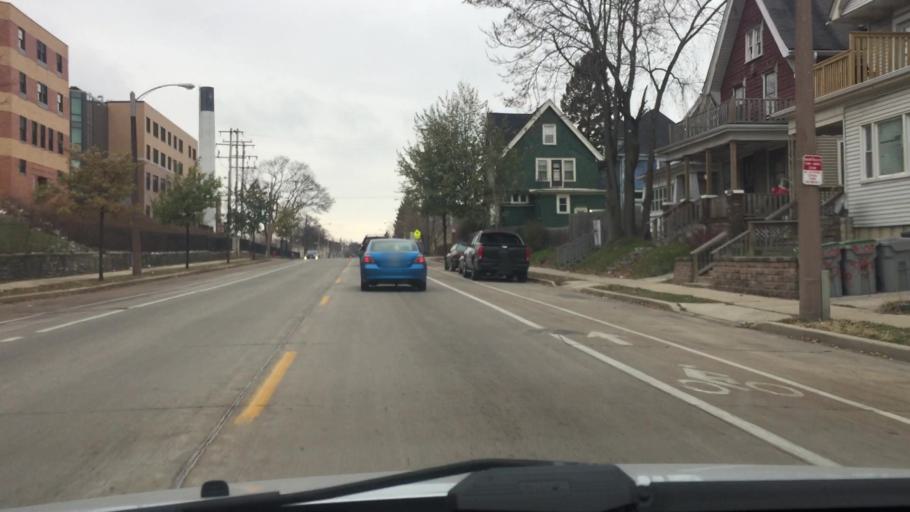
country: US
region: Wisconsin
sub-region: Milwaukee County
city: Milwaukee
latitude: 43.0433
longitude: -87.9393
